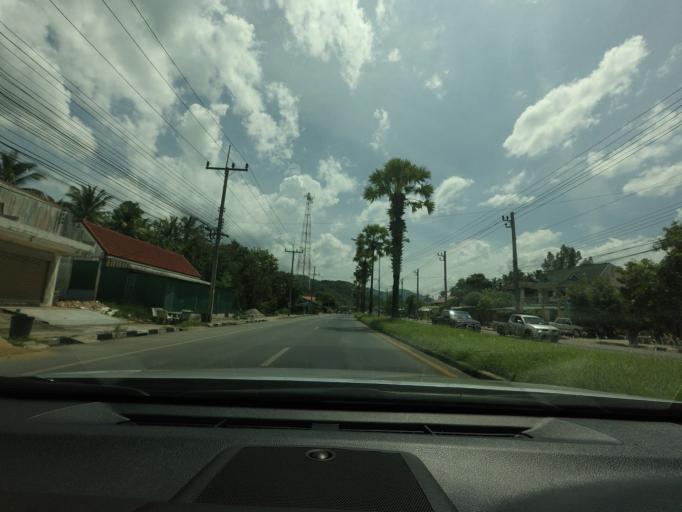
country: TH
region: Yala
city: Krong Pi Nang
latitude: 6.4581
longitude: 101.3374
